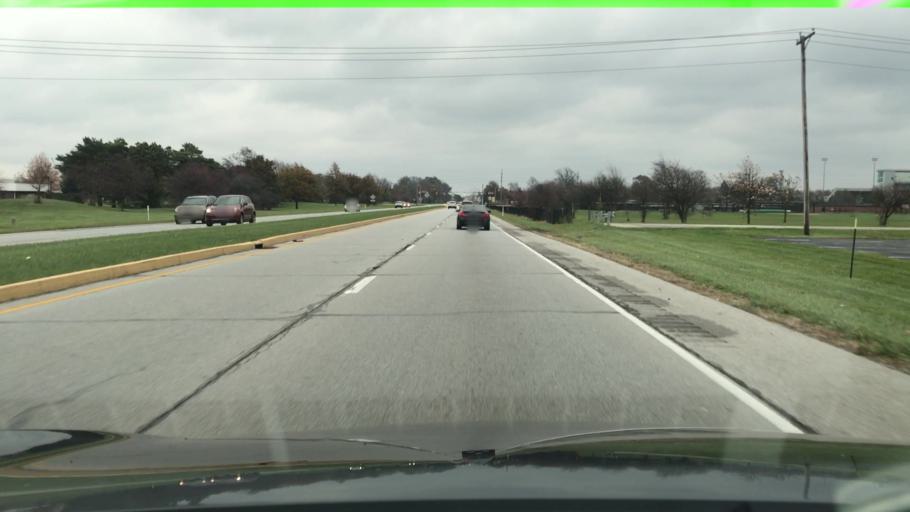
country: US
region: Indiana
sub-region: Delaware County
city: Muncie
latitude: 40.2189
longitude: -85.4252
